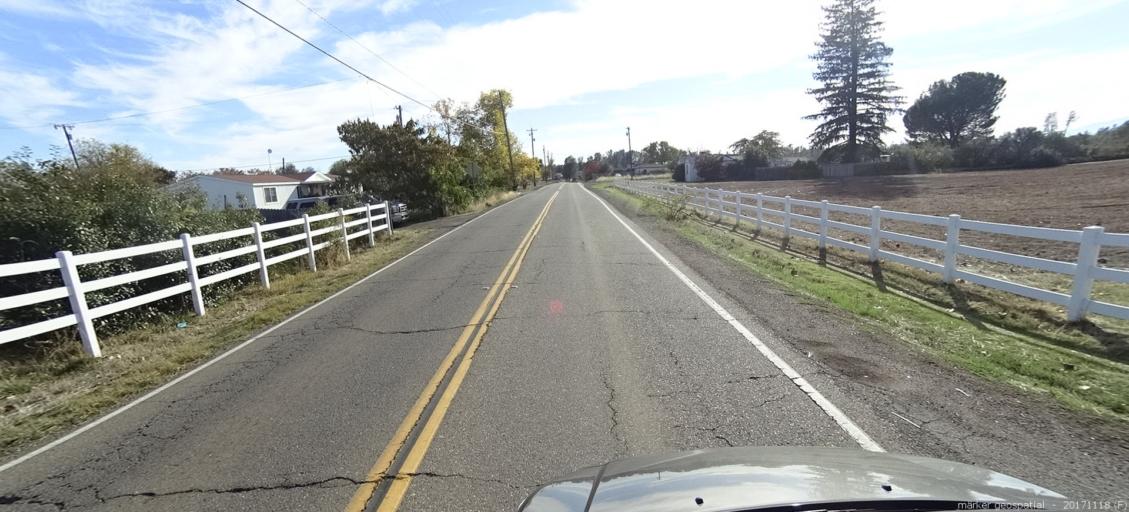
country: US
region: California
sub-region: Shasta County
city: Anderson
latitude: 40.4768
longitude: -122.3973
